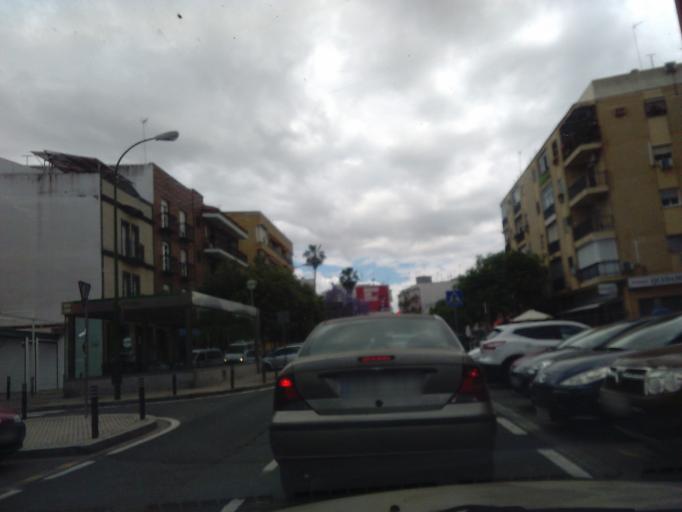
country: ES
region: Andalusia
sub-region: Provincia de Sevilla
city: Sevilla
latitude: 37.3718
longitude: -5.9519
